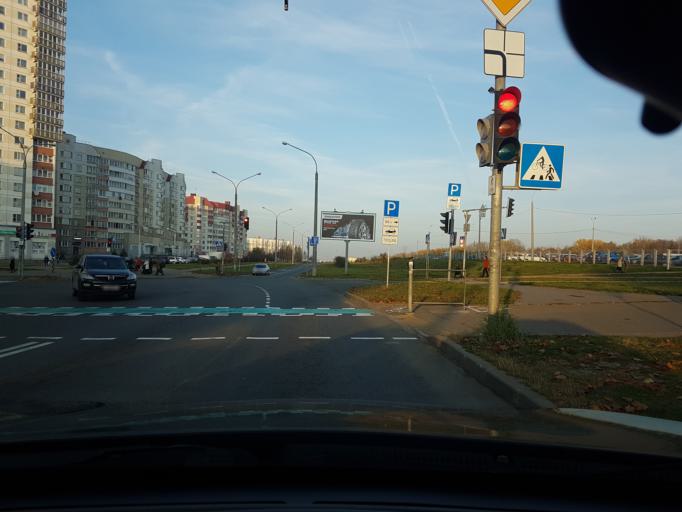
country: BY
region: Minsk
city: Shchomyslitsa
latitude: 53.8461
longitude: 27.4870
